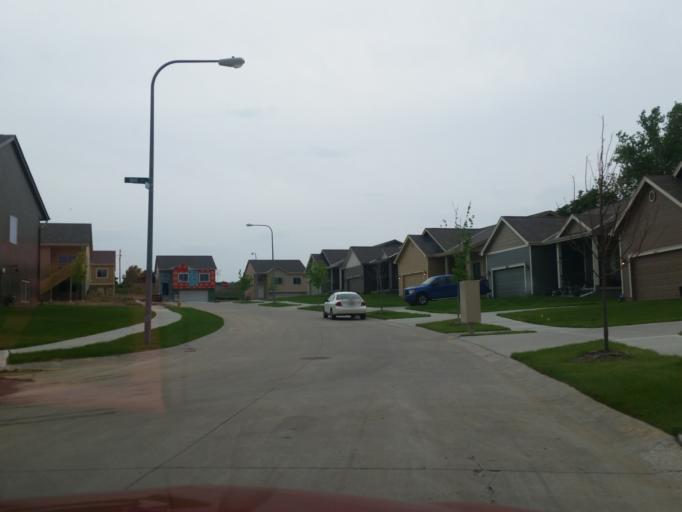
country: US
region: Nebraska
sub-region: Douglas County
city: Bennington
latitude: 41.3228
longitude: -96.1305
